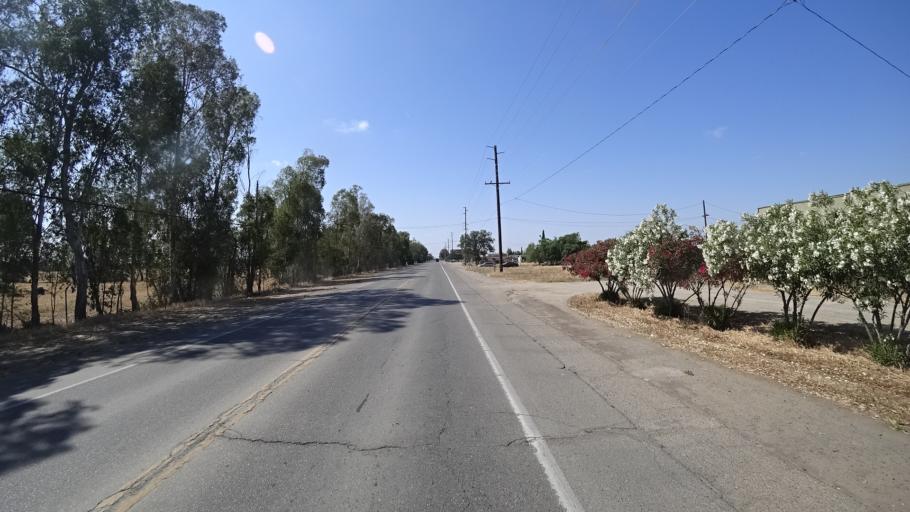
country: US
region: California
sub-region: Kings County
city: Home Garden
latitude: 36.3106
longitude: -119.6370
